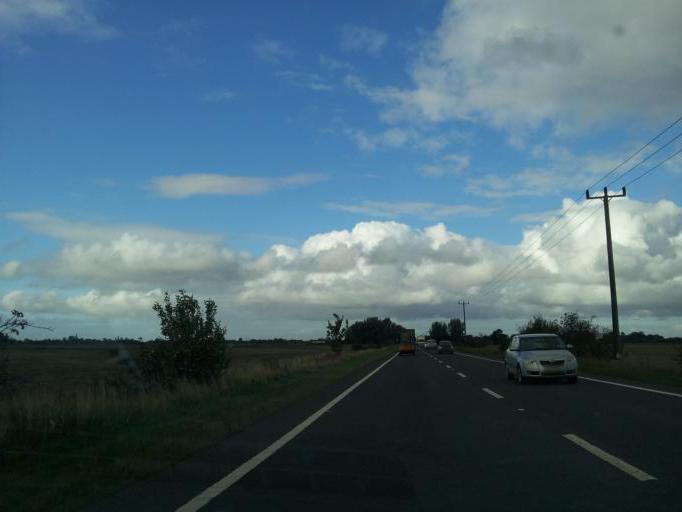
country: GB
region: England
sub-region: Norfolk
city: Clenchwarton
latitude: 52.7472
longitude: 0.3501
